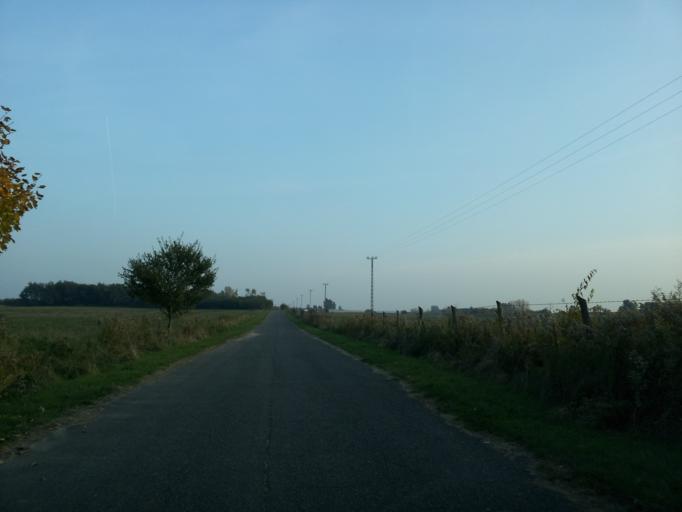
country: HU
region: Komarom-Esztergom
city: Kisber
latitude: 47.4712
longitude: 17.9514
